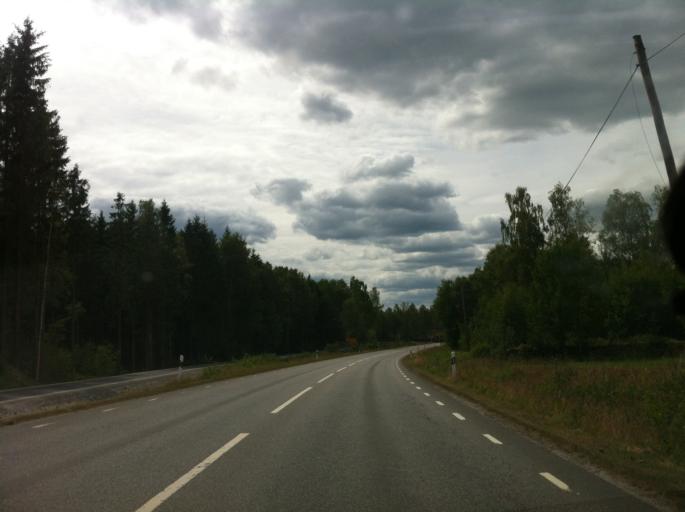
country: SE
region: Kronoberg
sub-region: Tingsryds Kommun
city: Tingsryd
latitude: 56.5309
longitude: 14.8670
